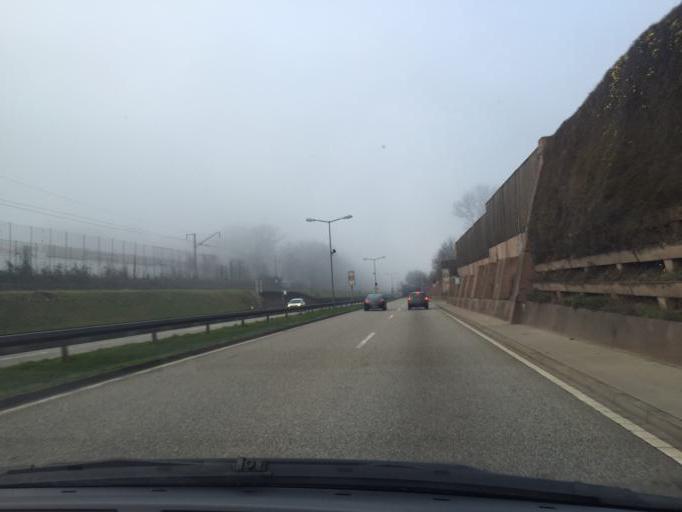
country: DE
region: Baden-Wuerttemberg
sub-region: Freiburg Region
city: Freiburg
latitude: 47.9846
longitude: 7.8824
